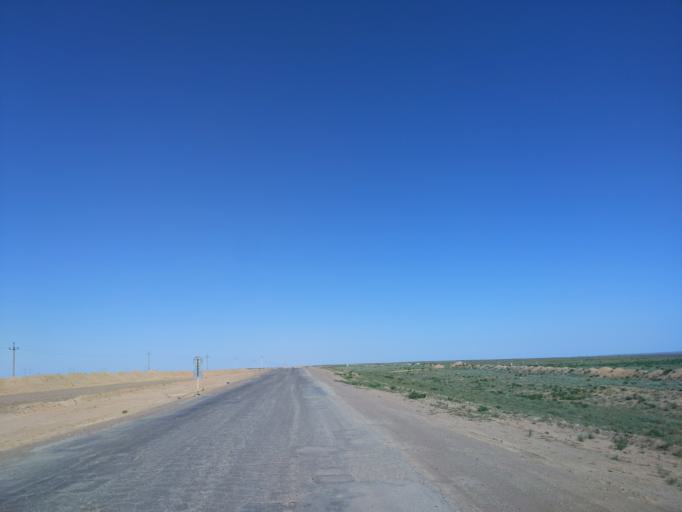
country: KZ
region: Almaty Oblysy
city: Bakanas
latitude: 44.1506
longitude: 75.8631
